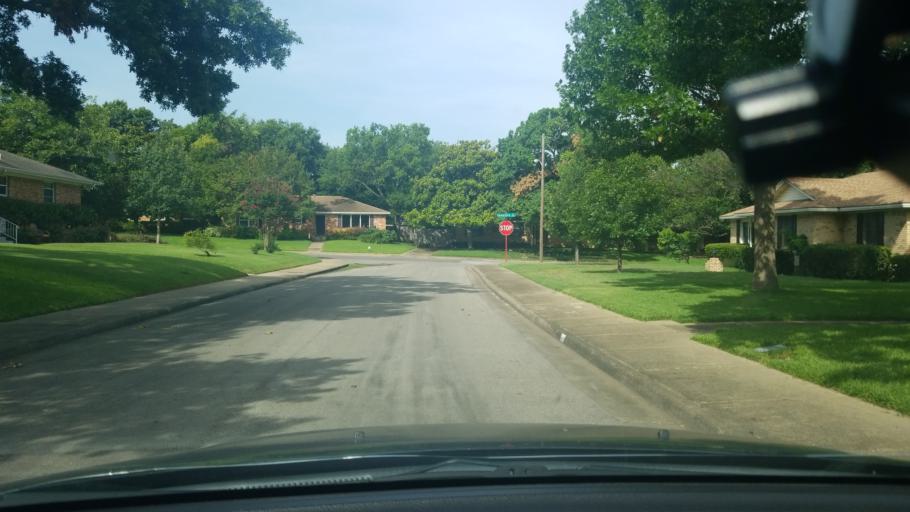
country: US
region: Texas
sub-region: Dallas County
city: Highland Park
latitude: 32.8073
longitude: -96.6982
